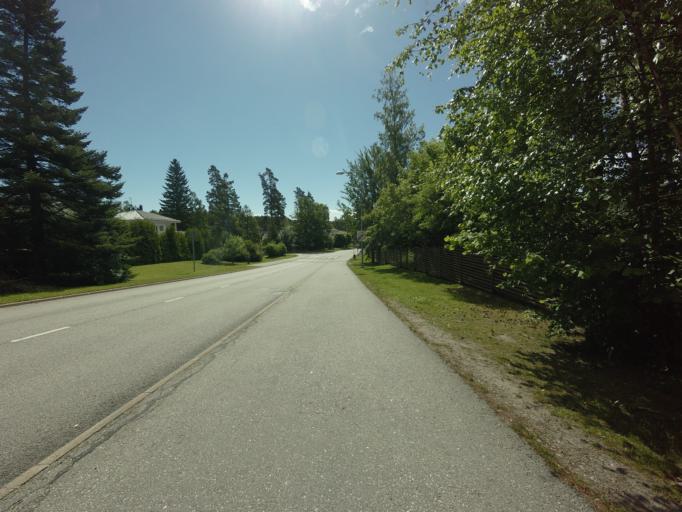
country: FI
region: Uusimaa
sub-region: Helsinki
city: Espoo
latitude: 60.1291
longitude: 24.6669
